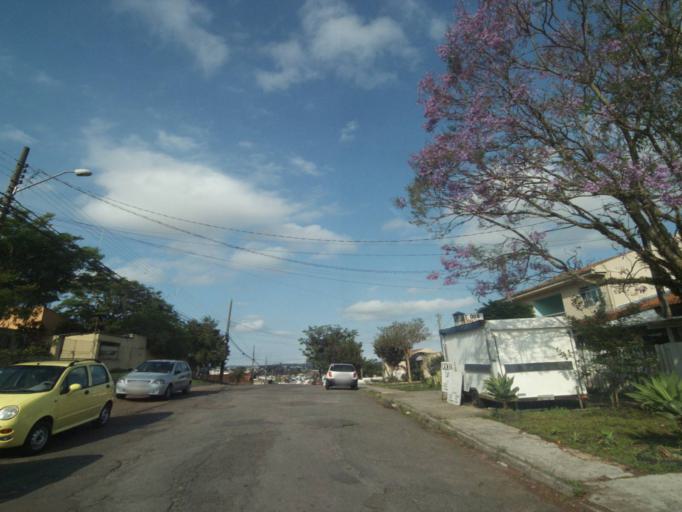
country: BR
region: Parana
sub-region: Pinhais
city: Pinhais
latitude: -25.4051
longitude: -49.1993
